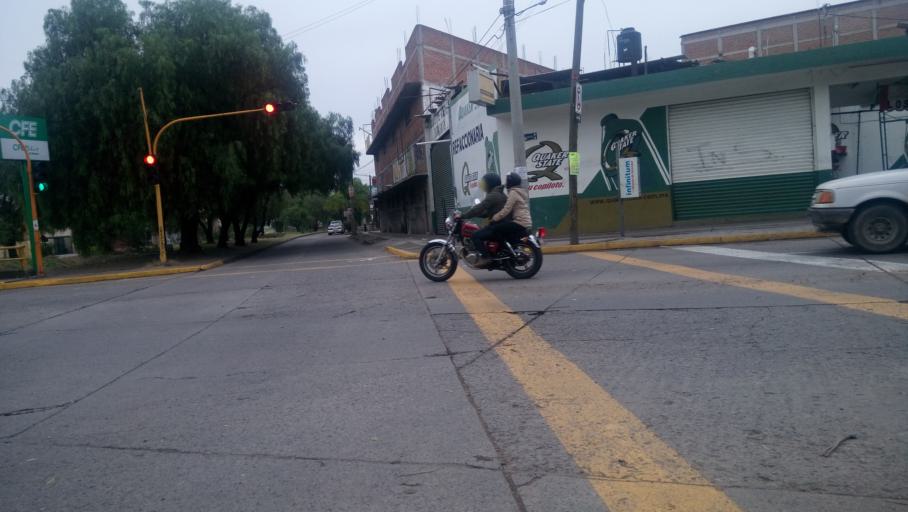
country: MX
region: Guanajuato
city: Leon
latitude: 21.1421
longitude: -101.6662
